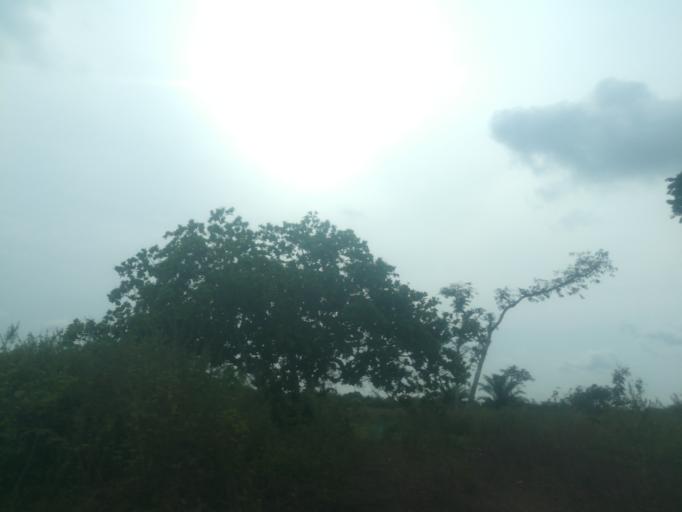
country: NG
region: Ogun
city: Ayetoro
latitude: 7.2973
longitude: 3.0772
